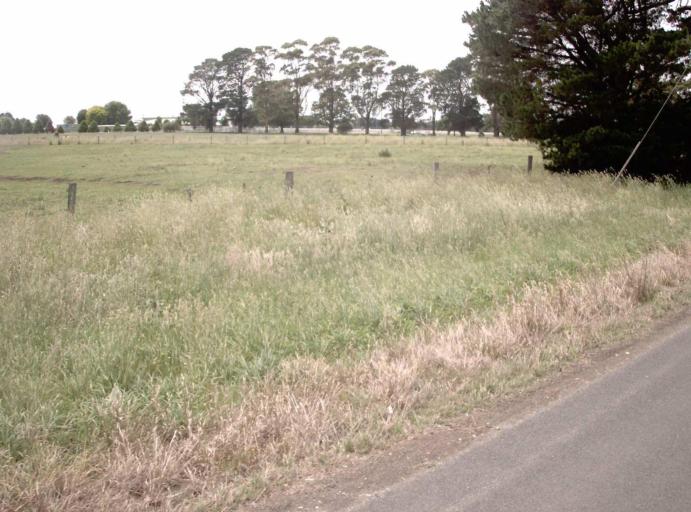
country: AU
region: Victoria
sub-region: Wellington
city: Sale
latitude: -38.0695
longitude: 147.0358
